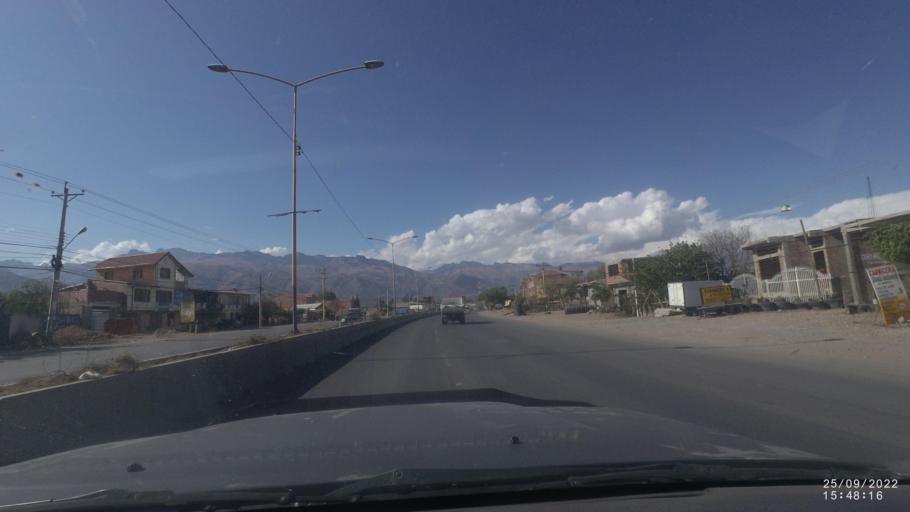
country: BO
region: Cochabamba
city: Sipe Sipe
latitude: -17.4137
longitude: -66.3344
